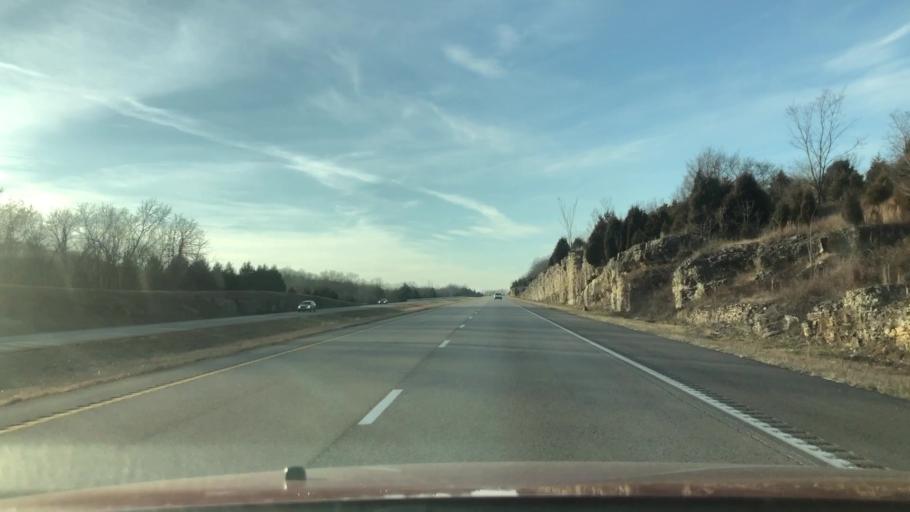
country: US
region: Missouri
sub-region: Wright County
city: Mansfield
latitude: 37.1122
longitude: -92.6590
